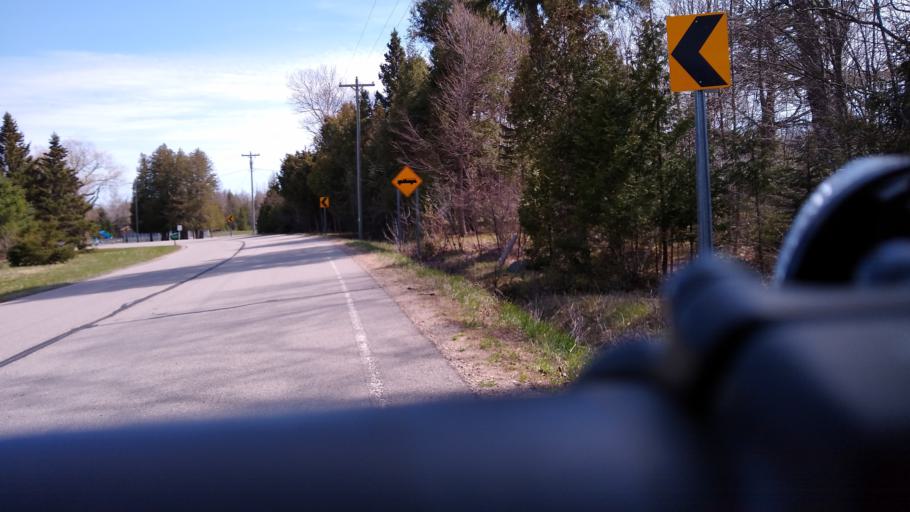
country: US
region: Michigan
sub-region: Delta County
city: Escanaba
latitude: 45.6874
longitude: -87.1524
